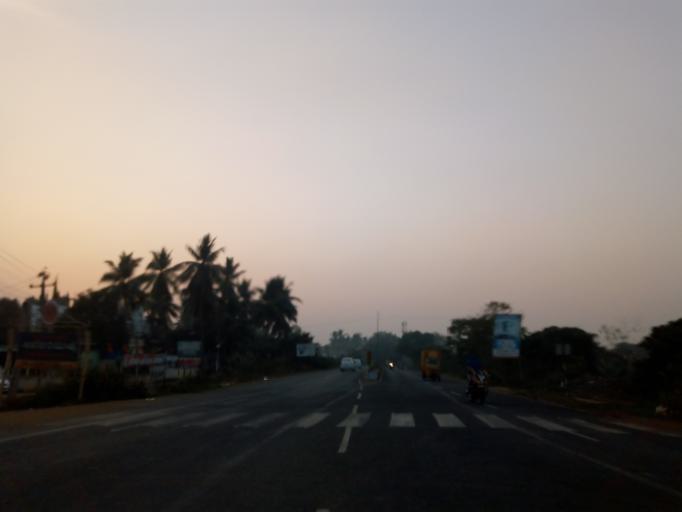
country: IN
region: Andhra Pradesh
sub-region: West Godavari
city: Tadepallegudem
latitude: 16.8108
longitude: 81.5138
